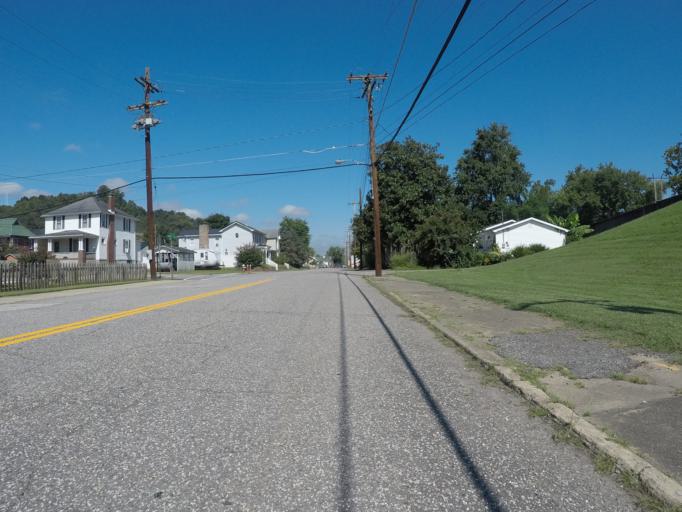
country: US
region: Ohio
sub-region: Lawrence County
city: South Point
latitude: 38.4202
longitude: -82.5986
